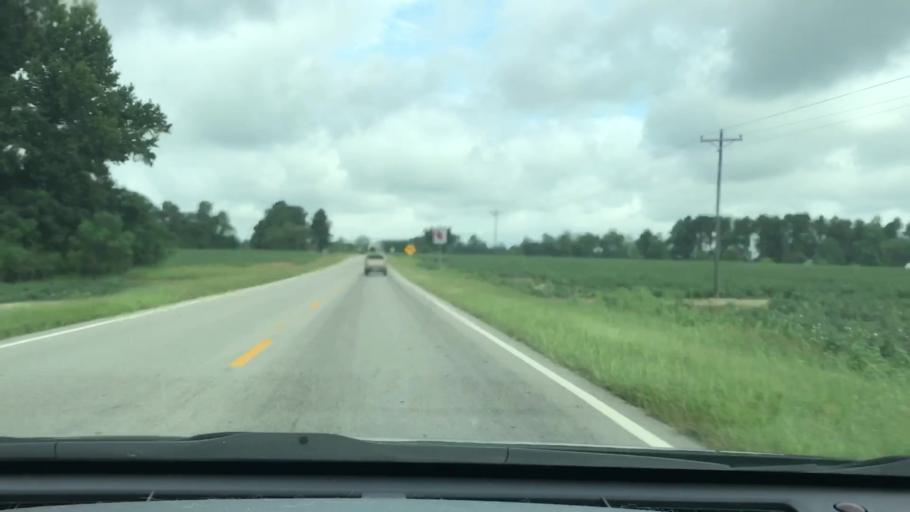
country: US
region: Georgia
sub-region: Jefferson County
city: Wrens
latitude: 33.2569
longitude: -82.4691
